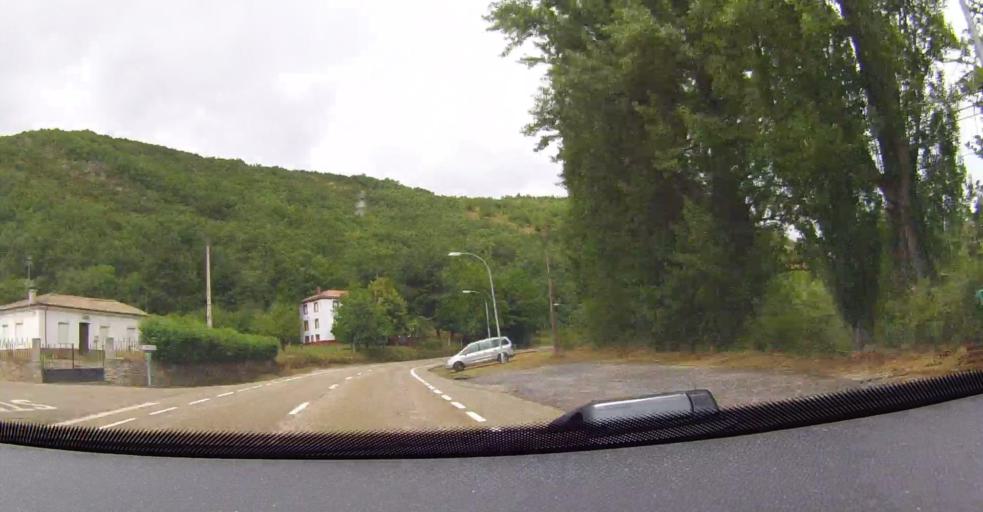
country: ES
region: Castille and Leon
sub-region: Provincia de Leon
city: Bonar
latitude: 42.8980
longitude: -5.3146
